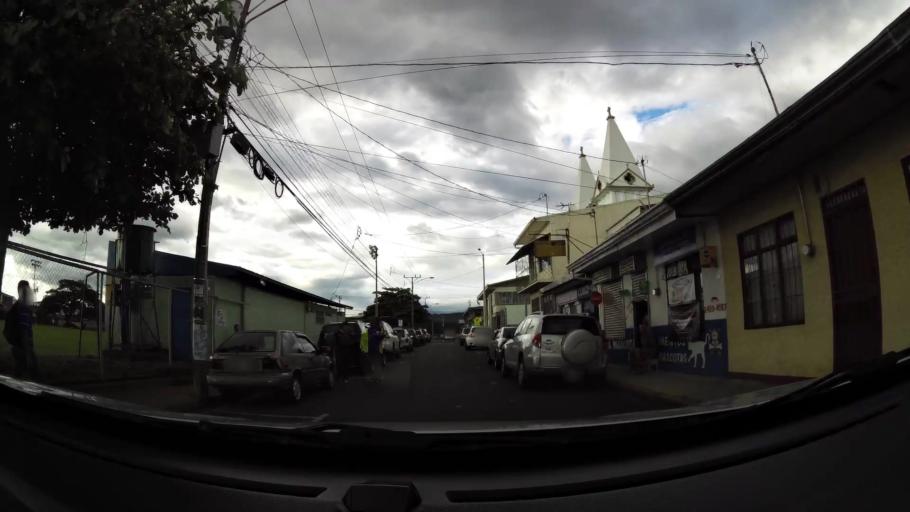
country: CR
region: Alajuela
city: Alajuela
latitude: 10.0182
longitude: -84.2166
